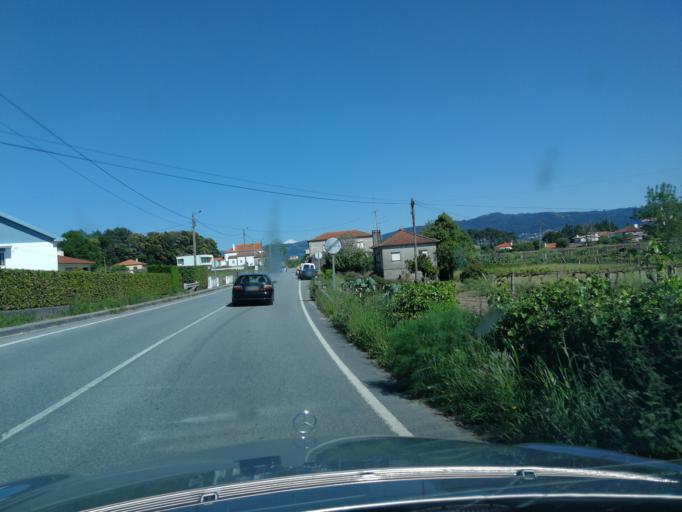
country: PT
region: Viana do Castelo
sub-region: Viana do Castelo
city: Darque
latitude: 41.7120
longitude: -8.7572
